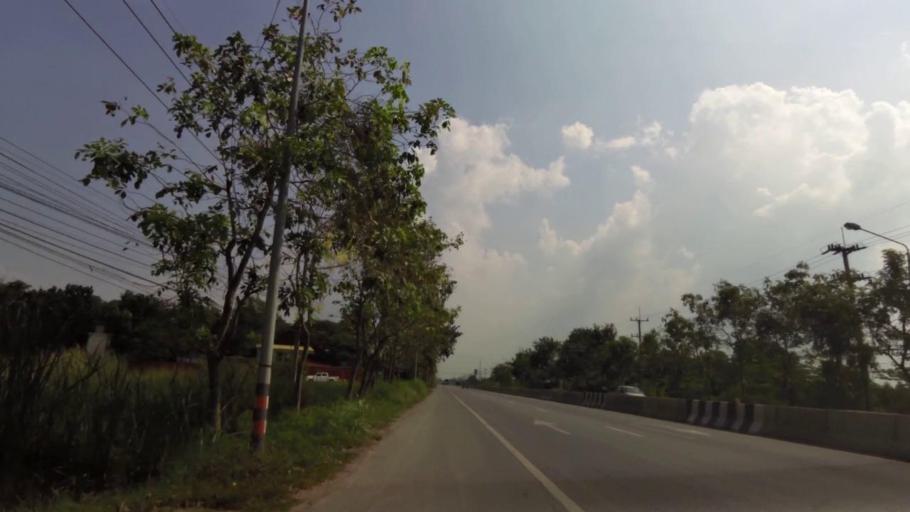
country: TH
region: Ang Thong
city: Ang Thong
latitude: 14.6035
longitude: 100.3978
